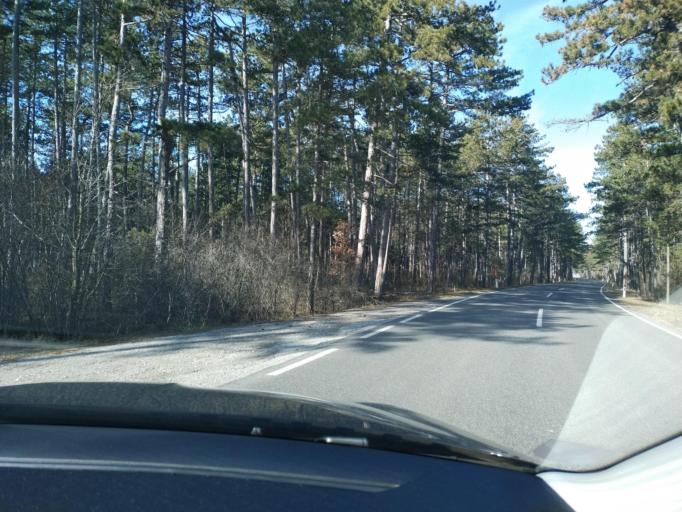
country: AT
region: Lower Austria
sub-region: Politischer Bezirk Neunkirchen
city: Breitenau
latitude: 47.7559
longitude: 16.1560
